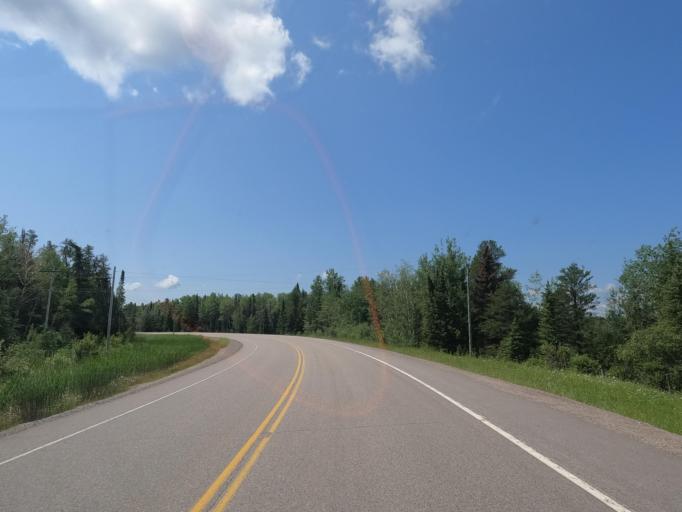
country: CA
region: Ontario
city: Dryden
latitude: 49.9239
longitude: -93.3589
